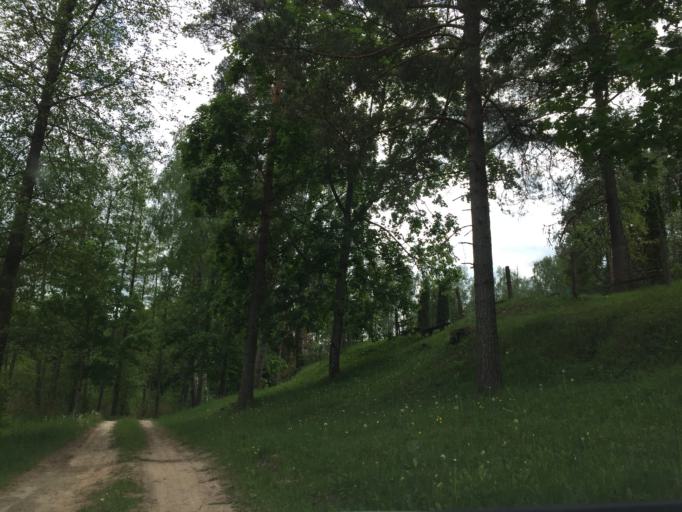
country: LV
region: Dagda
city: Dagda
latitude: 56.0881
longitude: 27.6988
